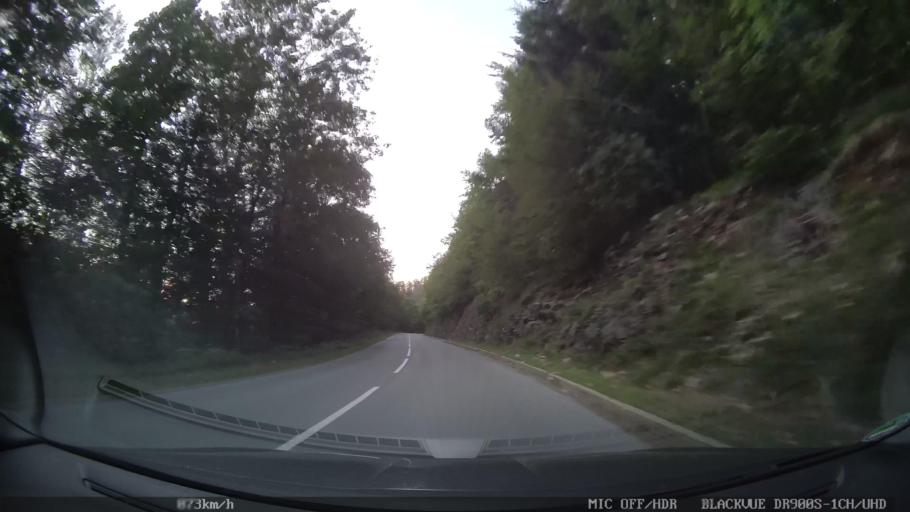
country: HR
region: Primorsko-Goranska
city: Novi Vinodolski
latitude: 45.1675
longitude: 14.9332
